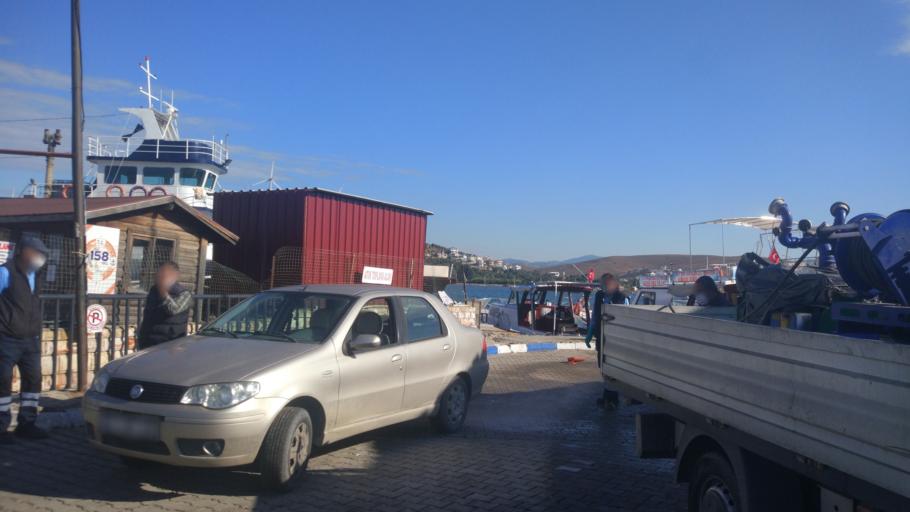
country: TR
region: Izmir
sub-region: Seferihisar
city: Seferhisar
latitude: 38.1947
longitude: 26.7841
